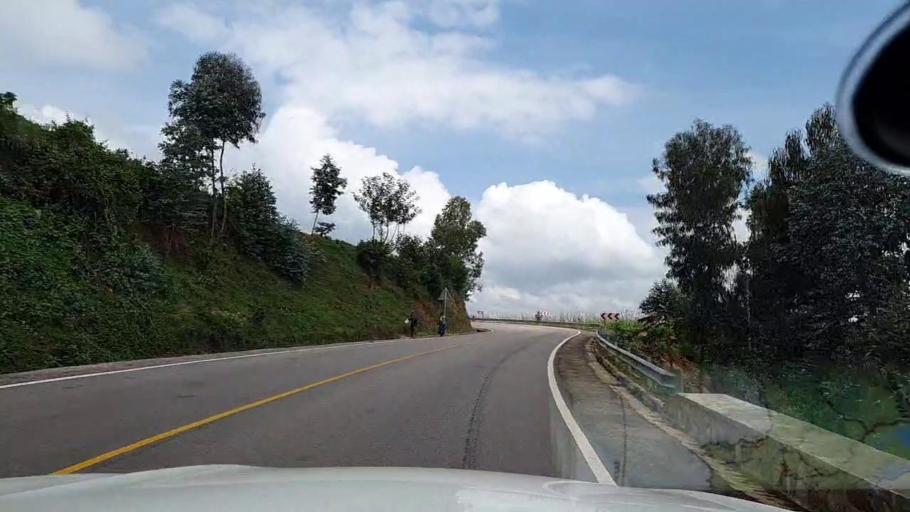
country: RW
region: Southern Province
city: Nzega
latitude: -2.5047
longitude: 29.5015
